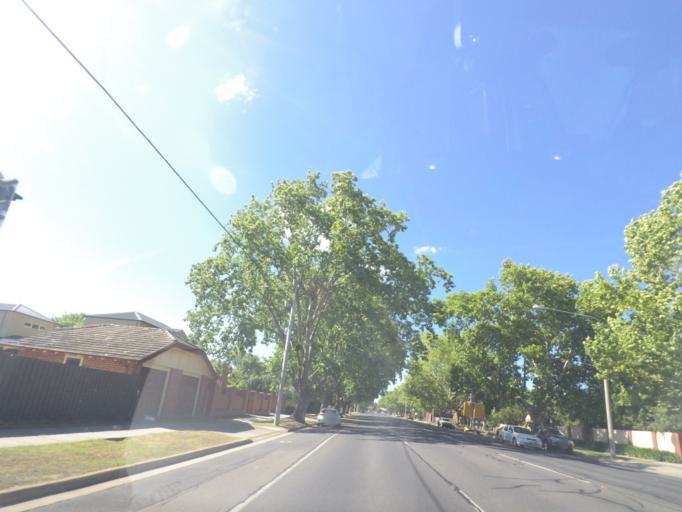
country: AU
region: New South Wales
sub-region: Albury Municipality
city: Albury
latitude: -36.0715
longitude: 146.9260
